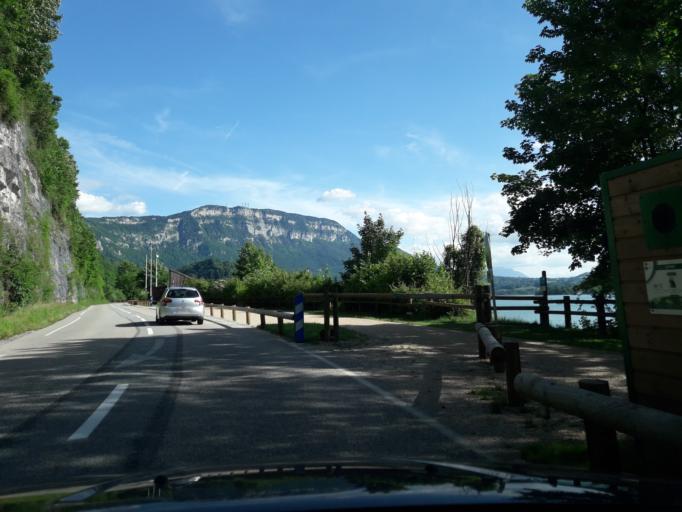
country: FR
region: Rhone-Alpes
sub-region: Departement de la Savoie
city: Novalaise
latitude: 45.5753
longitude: 5.8054
